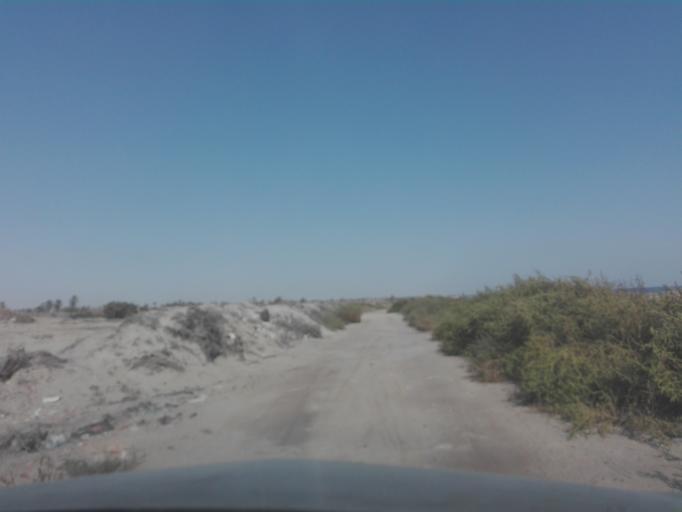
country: TN
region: Qabis
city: Gabes
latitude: 33.9656
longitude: 10.0643
